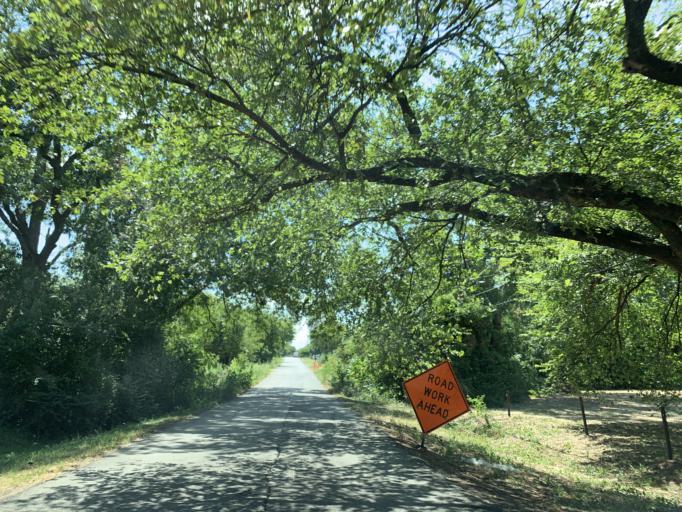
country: US
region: Texas
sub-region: Dallas County
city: Dallas
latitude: 32.7122
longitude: -96.7768
